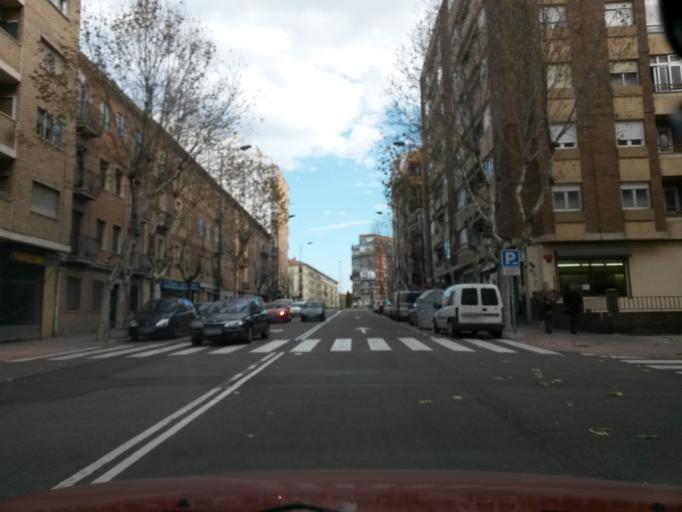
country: ES
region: Castille and Leon
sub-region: Provincia de Salamanca
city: Salamanca
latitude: 40.9678
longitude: -5.6486
